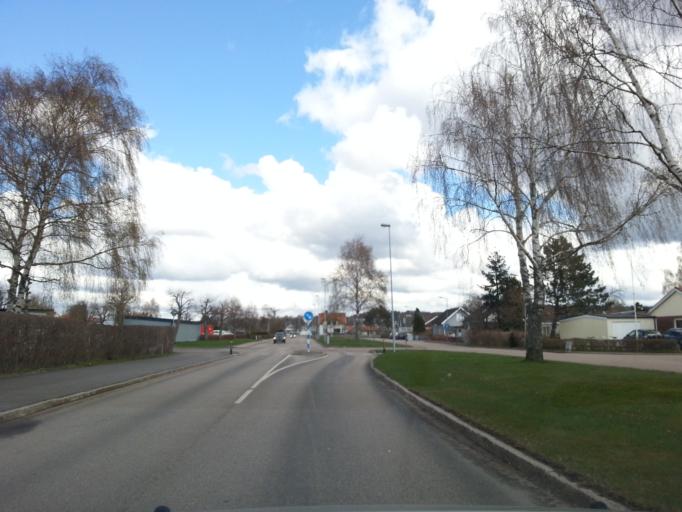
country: SE
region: Vaestra Goetaland
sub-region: Kungalvs Kommun
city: Kungalv
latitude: 57.8652
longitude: 11.9598
